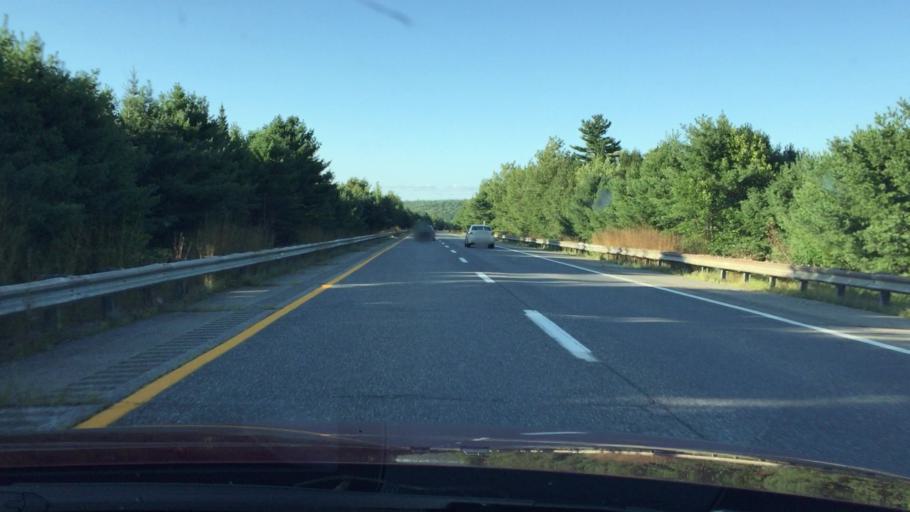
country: US
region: Maine
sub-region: Penobscot County
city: Medway
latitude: 45.6231
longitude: -68.5074
